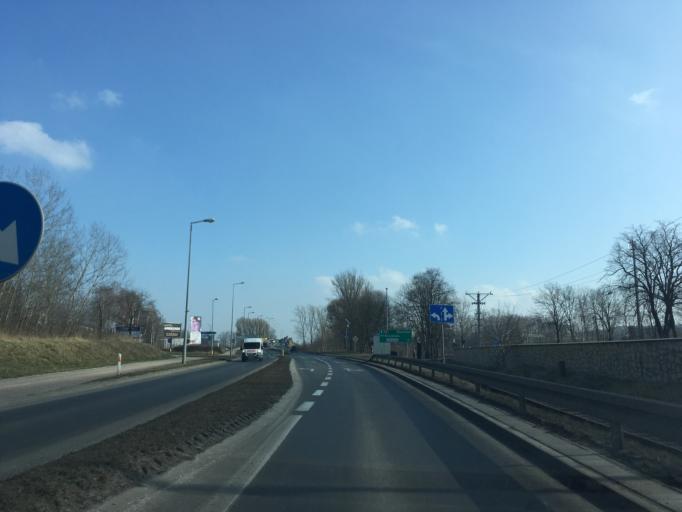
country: PL
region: Lower Silesian Voivodeship
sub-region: Powiat boleslawiecki
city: Boleslawiec
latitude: 51.2689
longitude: 15.5744
